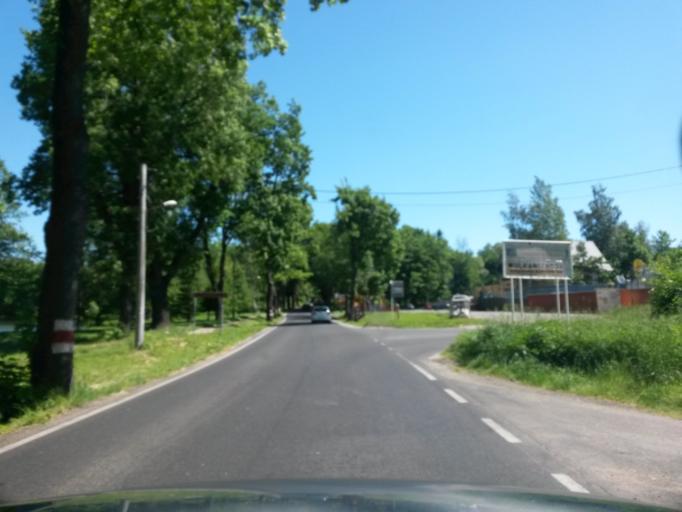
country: PL
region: Lower Silesian Voivodeship
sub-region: Powiat jeleniogorski
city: Kowary
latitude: 50.7973
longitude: 15.8221
